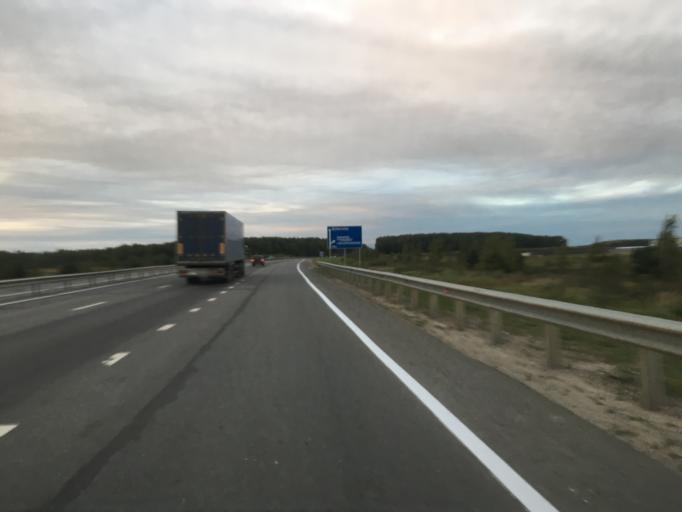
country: RU
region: Kaluga
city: Kaluga
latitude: 54.5690
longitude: 36.3347
